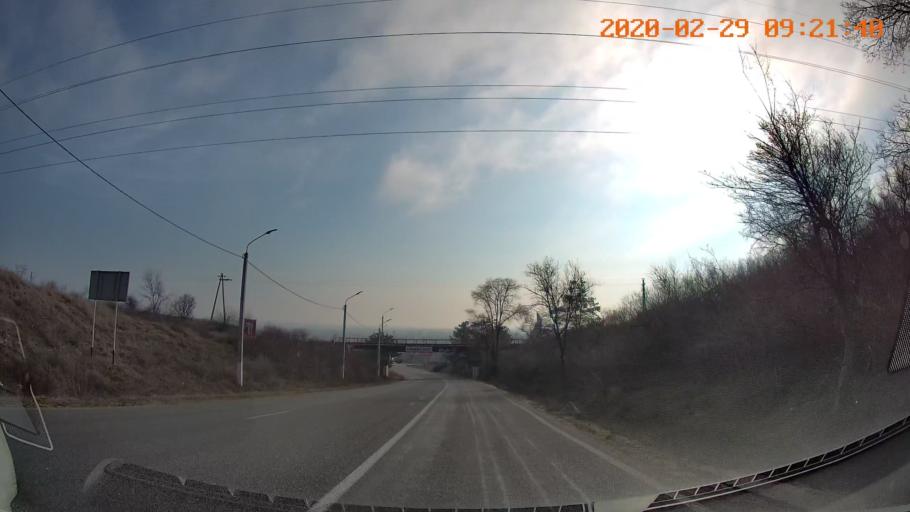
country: MD
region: Telenesti
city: Pervomaisc
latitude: 46.7382
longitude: 29.9616
